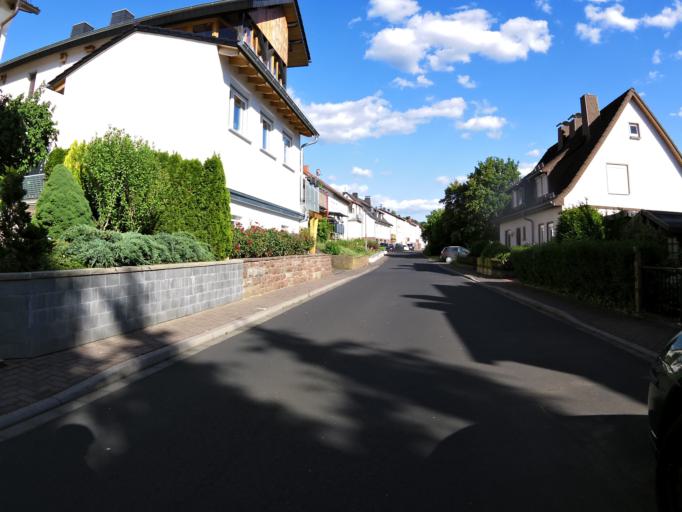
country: DE
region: Hesse
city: Philippsthal
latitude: 50.8409
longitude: 10.0085
